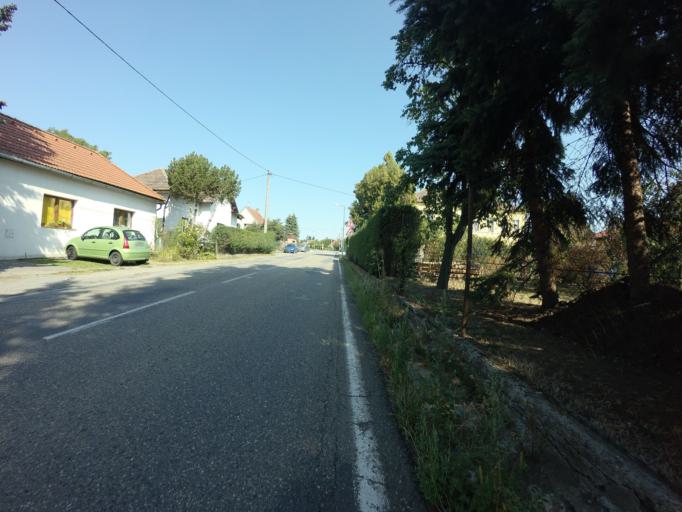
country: CZ
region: Central Bohemia
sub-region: Okres Benesov
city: Benesov
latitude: 49.7998
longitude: 14.6553
